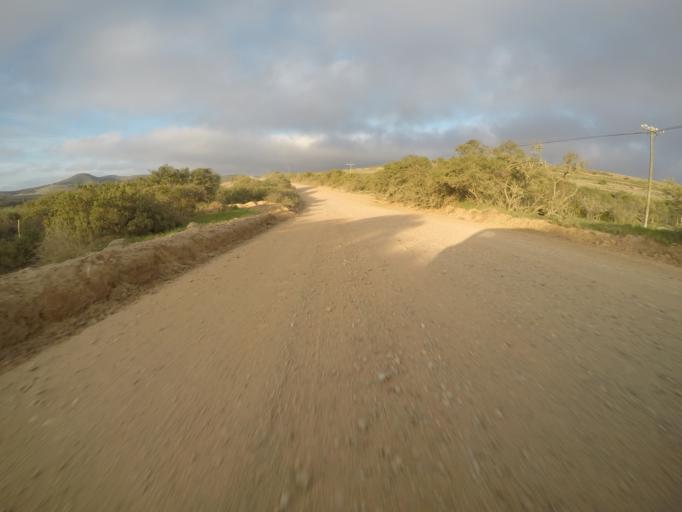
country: ZA
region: Western Cape
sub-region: Eden District Municipality
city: Mossel Bay
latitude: -34.1100
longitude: 22.0598
